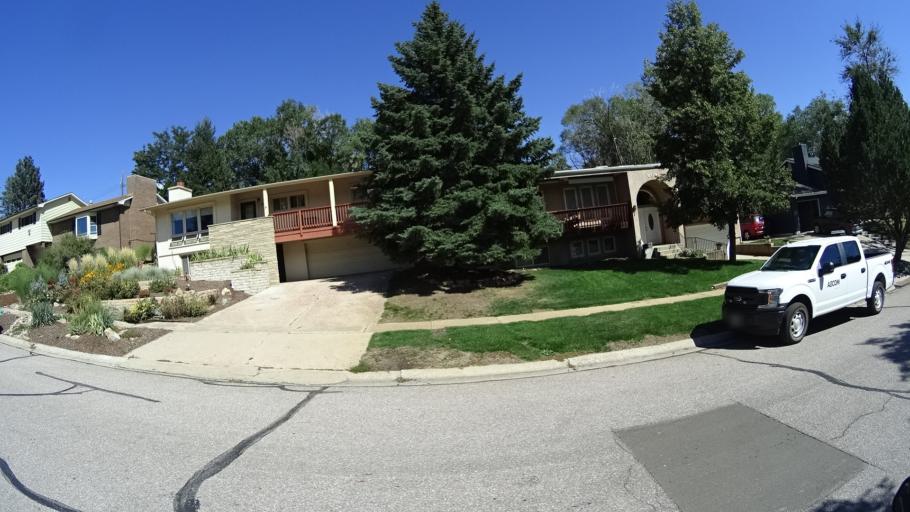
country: US
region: Colorado
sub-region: El Paso County
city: Colorado Springs
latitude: 38.8615
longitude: -104.8621
